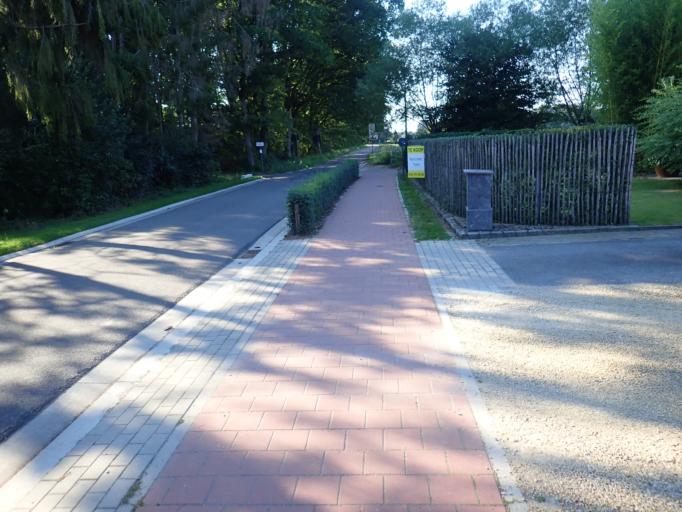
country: BE
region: Flanders
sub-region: Provincie Antwerpen
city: Hulshout
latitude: 51.0804
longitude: 4.7881
